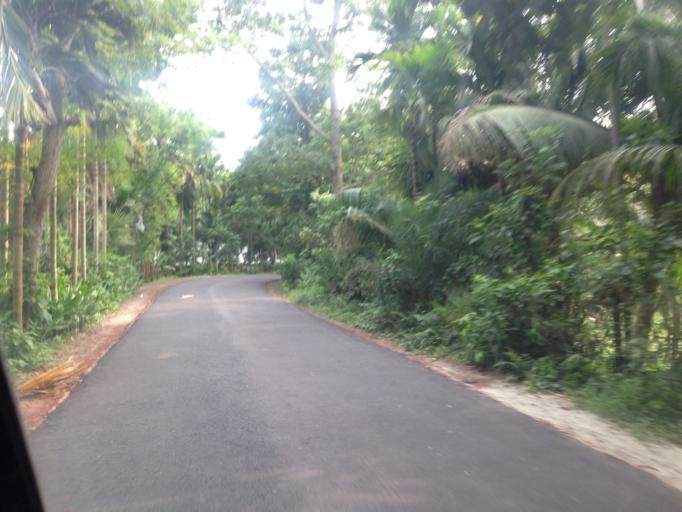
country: BD
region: Chittagong
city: Raipur
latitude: 23.0377
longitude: 90.7264
